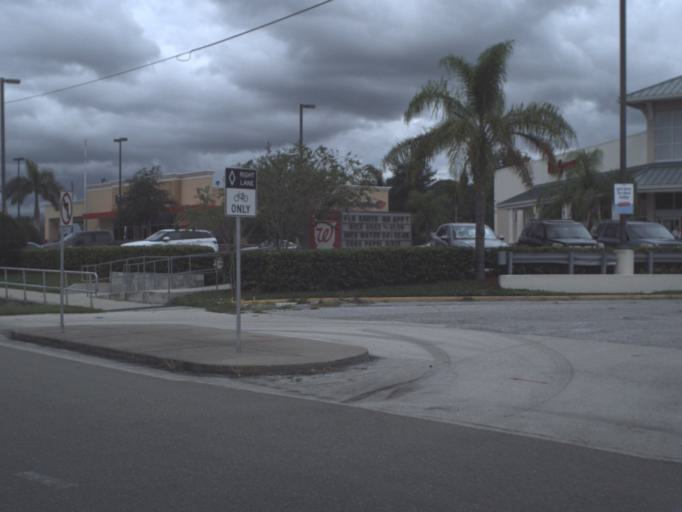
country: US
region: Florida
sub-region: Sarasota County
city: Laurel
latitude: 27.1385
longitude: -82.4581
